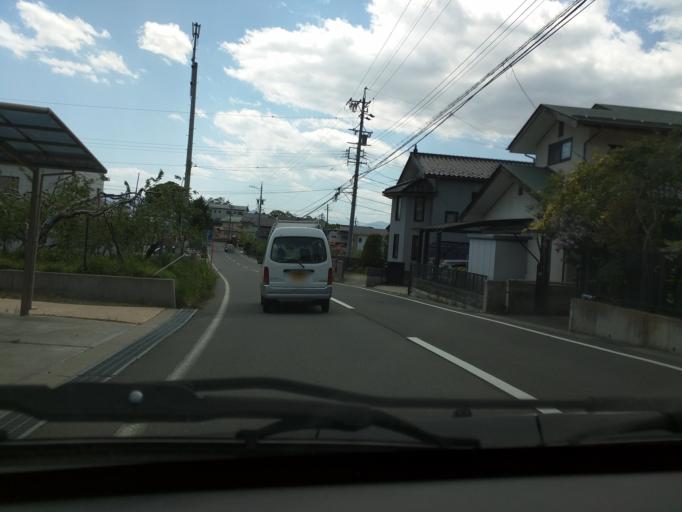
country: JP
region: Nagano
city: Nagano-shi
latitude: 36.6629
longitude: 138.1774
